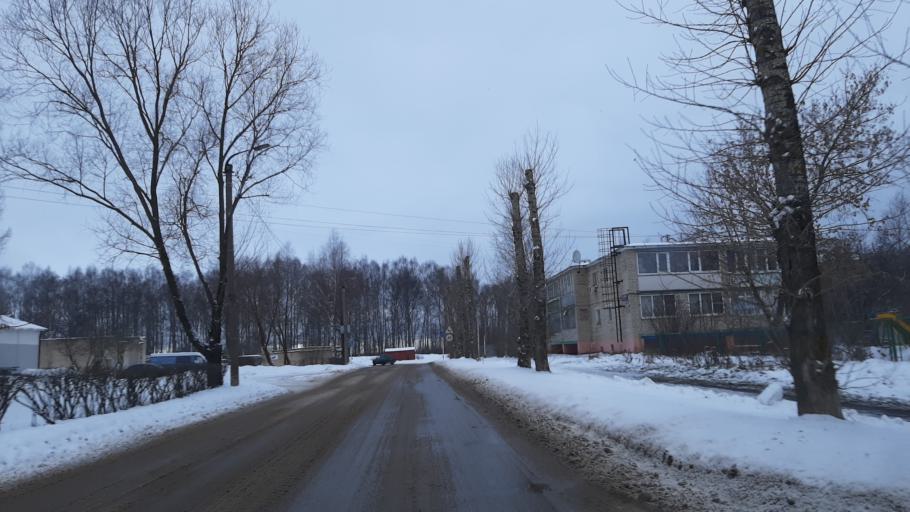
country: RU
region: Kostroma
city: Volgorechensk
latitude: 57.4439
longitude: 41.1463
